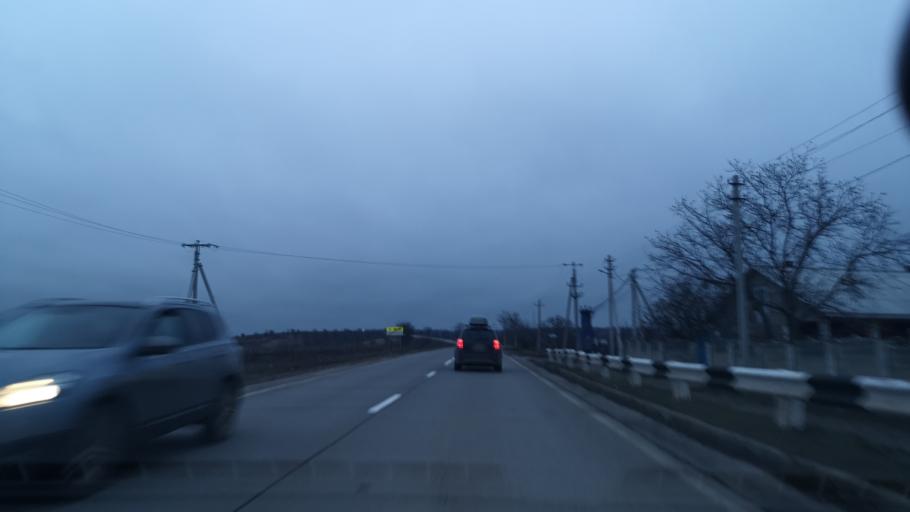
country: MD
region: Straseni
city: Straseni
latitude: 47.2851
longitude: 28.5805
